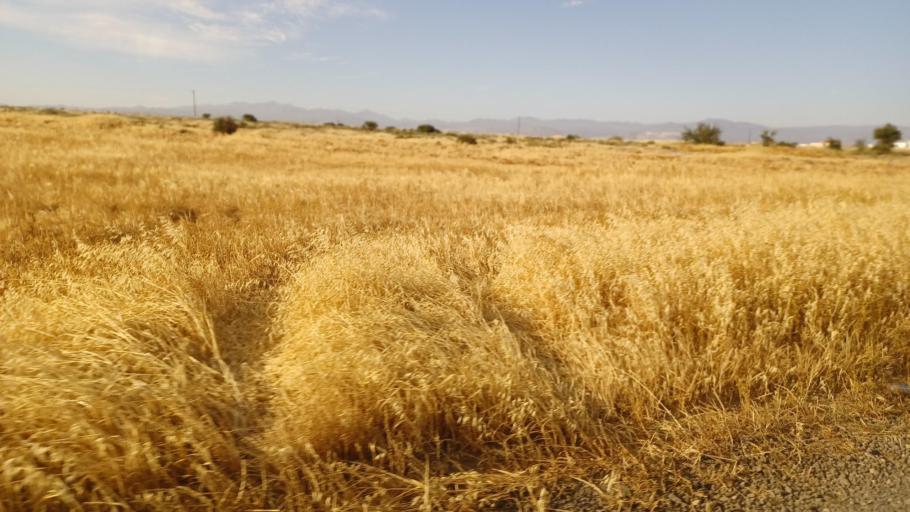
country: CY
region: Lefkosia
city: Mammari
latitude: 35.1692
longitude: 33.2105
